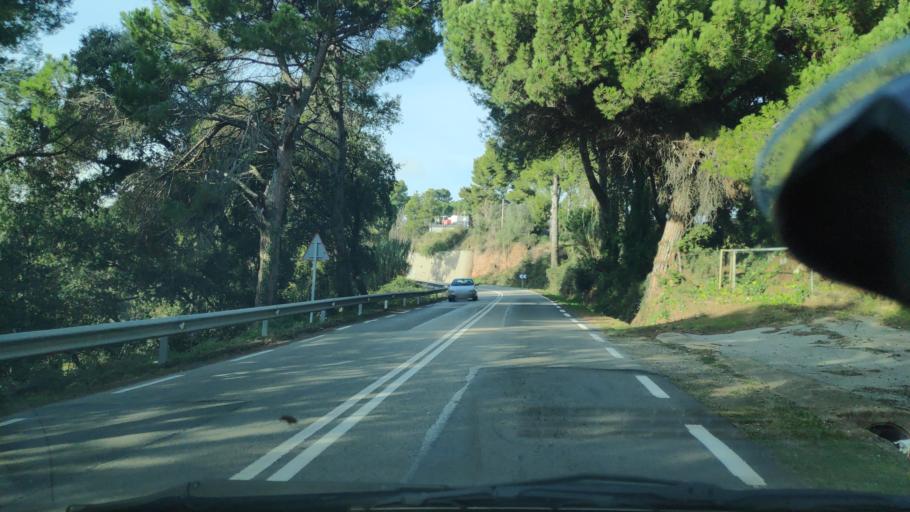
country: ES
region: Catalonia
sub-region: Provincia de Barcelona
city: Matadepera
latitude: 41.5937
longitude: 2.0403
